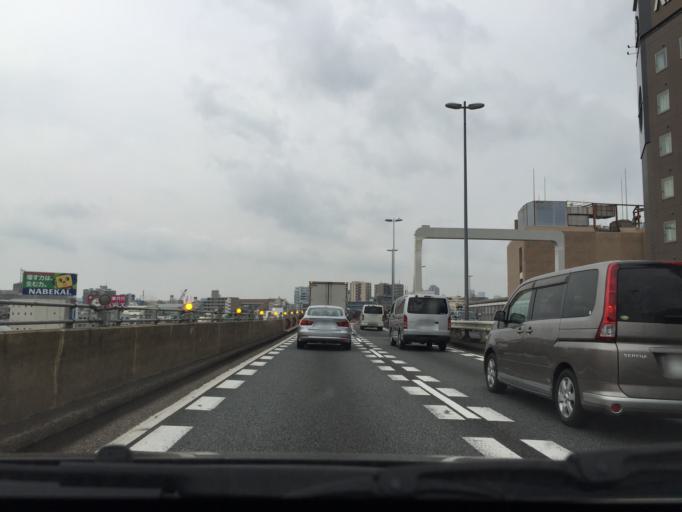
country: JP
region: Tokyo
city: Urayasu
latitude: 35.6869
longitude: 139.7915
